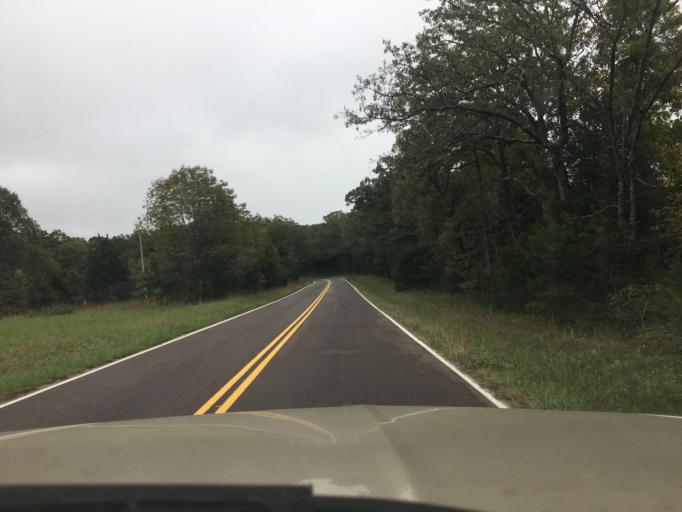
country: US
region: Missouri
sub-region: Crawford County
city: Cuba
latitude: 38.1945
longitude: -91.4632
